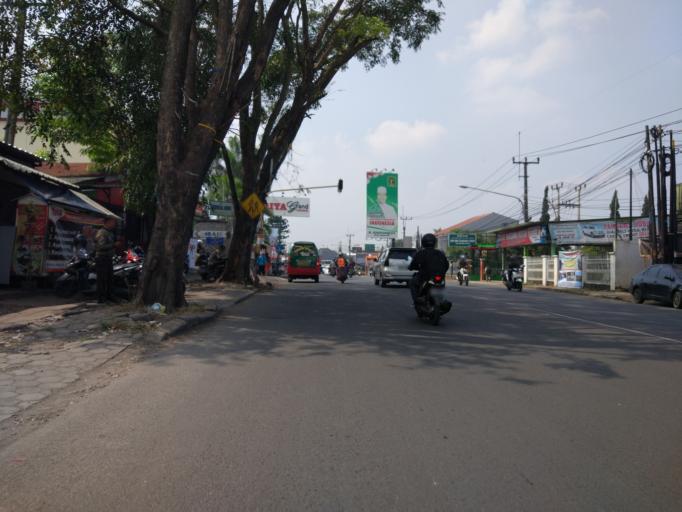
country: ID
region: West Java
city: Cileunyi
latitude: -6.9380
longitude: 107.7331
